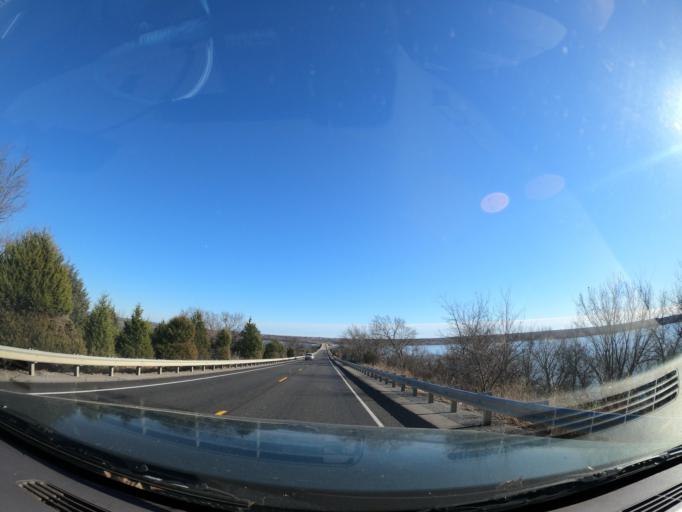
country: US
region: Oklahoma
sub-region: McIntosh County
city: Eufaula
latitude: 35.2491
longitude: -95.5693
